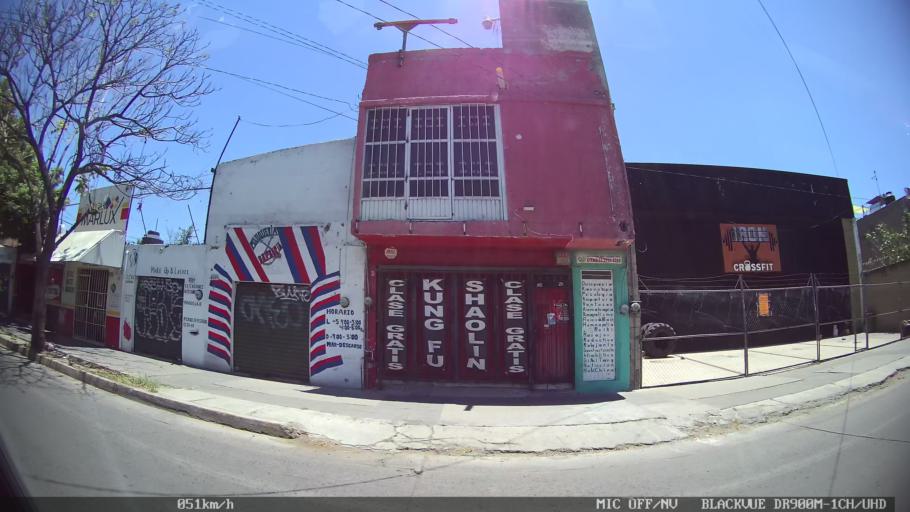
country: MX
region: Jalisco
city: Tlaquepaque
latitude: 20.6626
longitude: -103.2860
